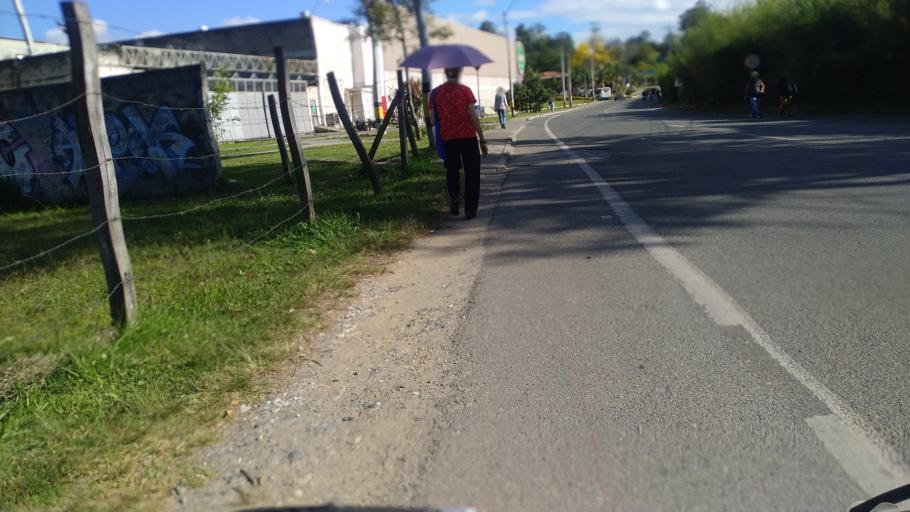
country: CO
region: Antioquia
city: Rionegro
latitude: 6.1429
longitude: -75.3801
